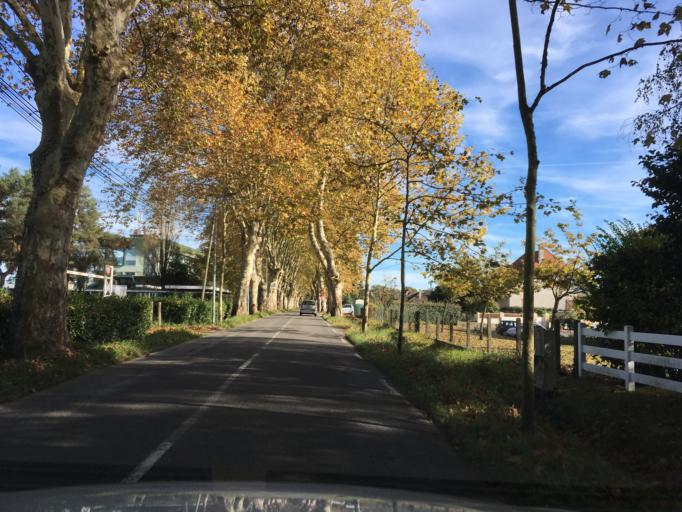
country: FR
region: Aquitaine
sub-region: Departement des Pyrenees-Atlantiques
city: Lons
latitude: 43.3348
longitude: -0.3766
